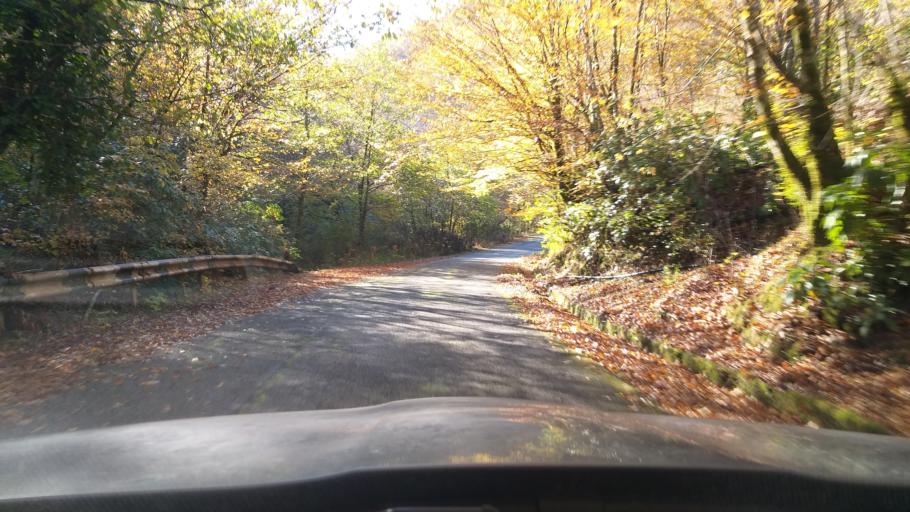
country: GE
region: Abkhazia
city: Bich'vinta
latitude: 43.1889
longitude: 40.4539
